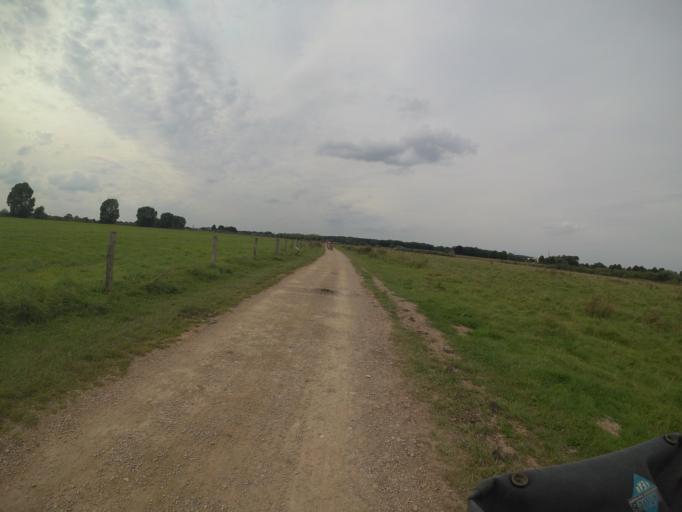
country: NL
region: Limburg
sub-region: Gemeente Gennep
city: Gennep
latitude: 51.7101
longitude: 5.9597
